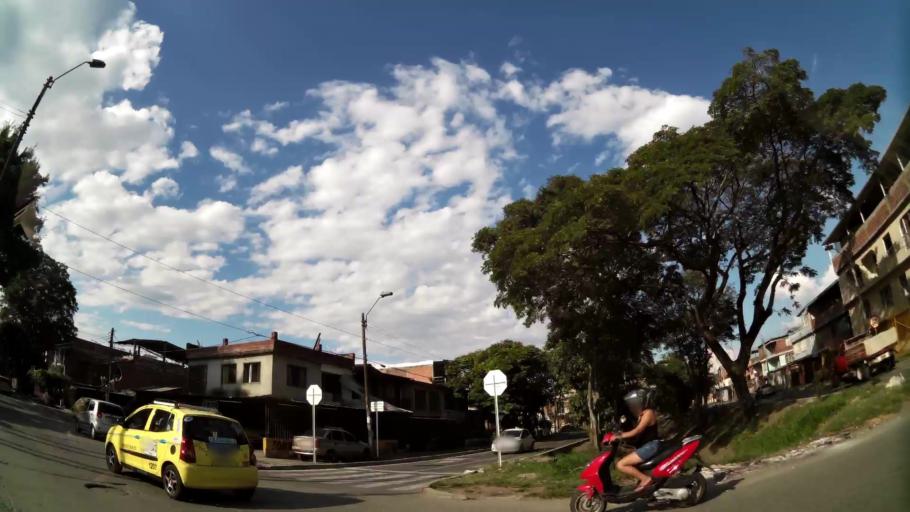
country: CO
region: Valle del Cauca
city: Cali
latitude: 3.4091
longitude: -76.5116
